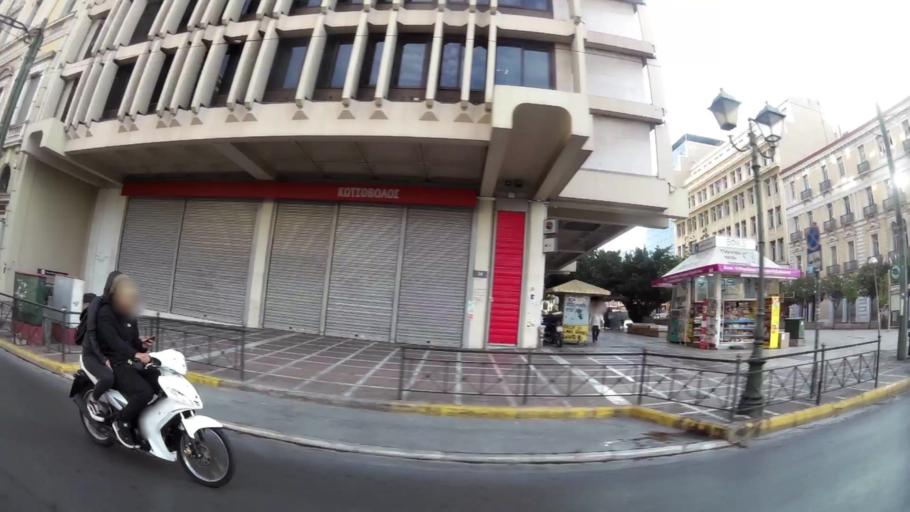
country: GR
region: Attica
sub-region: Nomarchia Athinas
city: Athens
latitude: 37.9798
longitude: 23.7318
